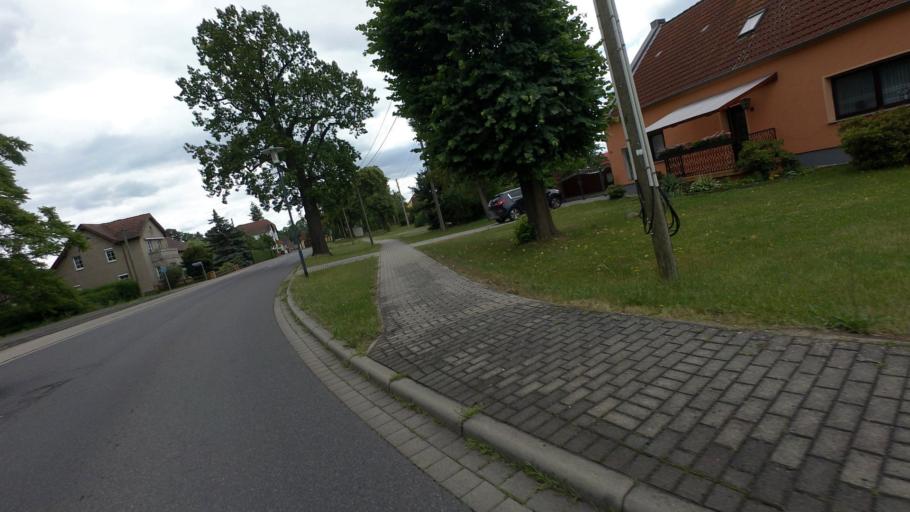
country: DE
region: Brandenburg
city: Crinitz
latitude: 51.8092
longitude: 13.8178
